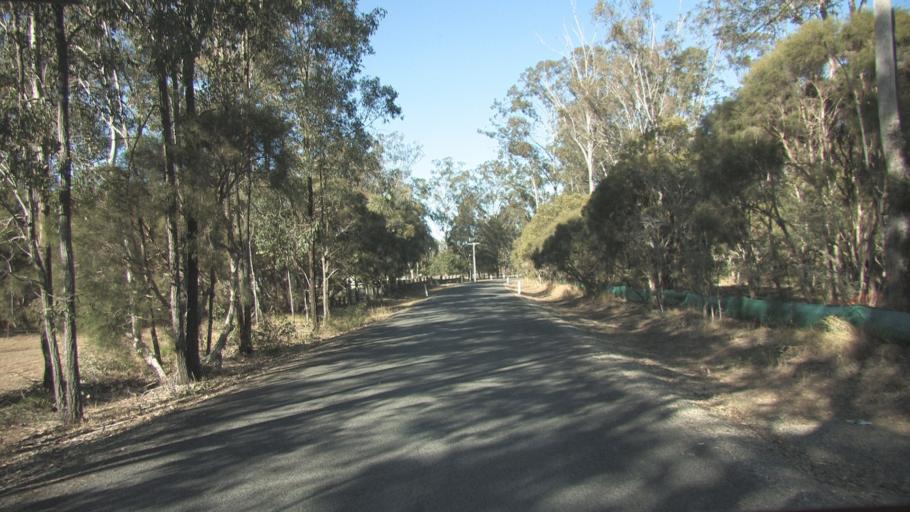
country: AU
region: Queensland
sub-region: Logan
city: Cedar Vale
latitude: -27.8406
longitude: 153.0026
